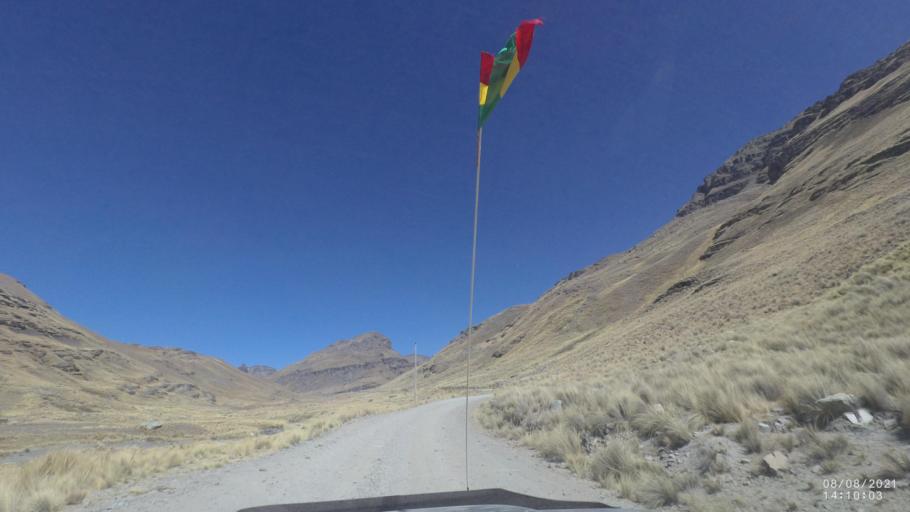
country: BO
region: Cochabamba
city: Sipe Sipe
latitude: -17.1500
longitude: -66.4357
